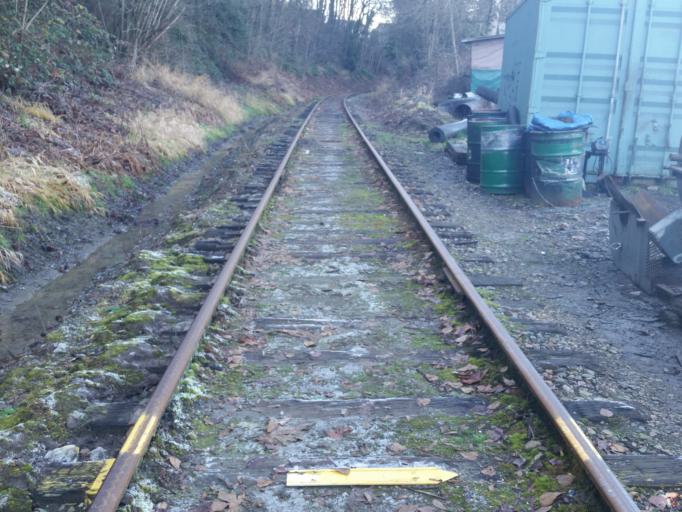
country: US
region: Washington
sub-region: King County
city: Woodinville
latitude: 47.7496
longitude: -122.1677
